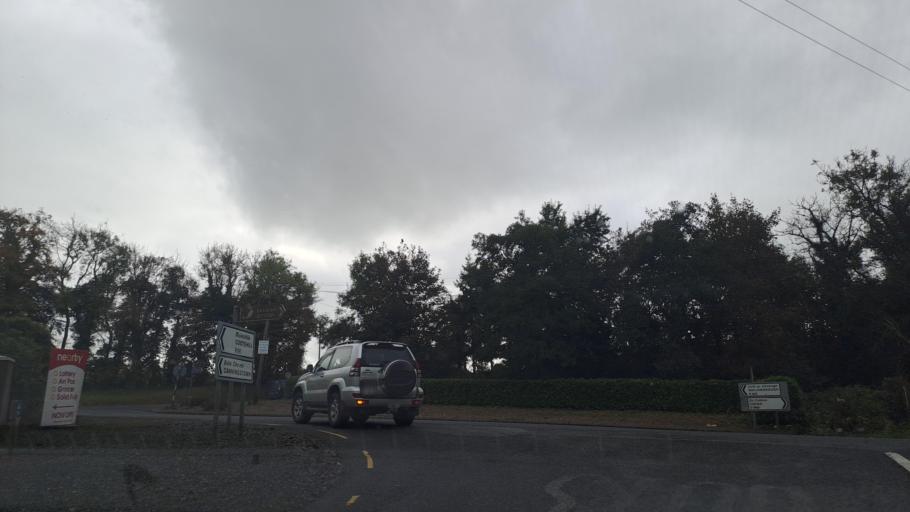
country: IE
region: Ulster
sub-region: An Cabhan
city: Bailieborough
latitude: 53.9267
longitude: -7.0045
